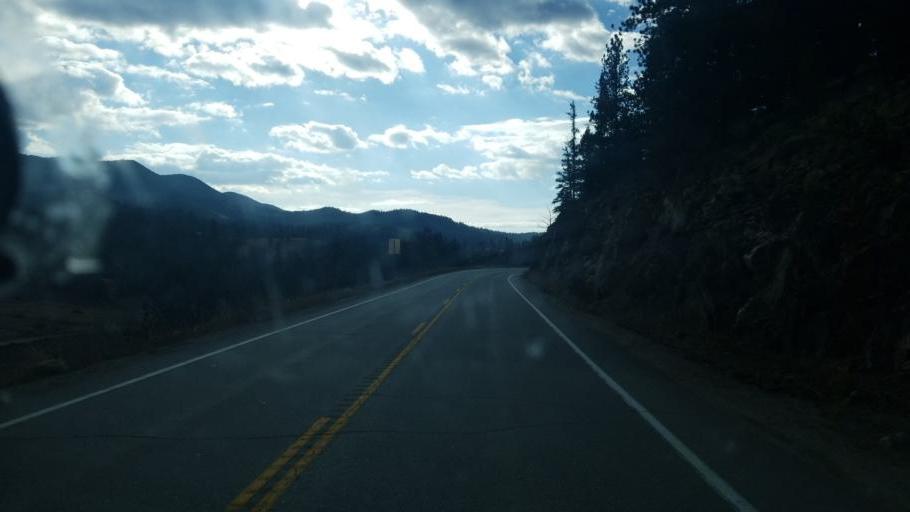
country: US
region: Colorado
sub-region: Chaffee County
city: Buena Vista
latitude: 38.8548
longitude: -105.9847
